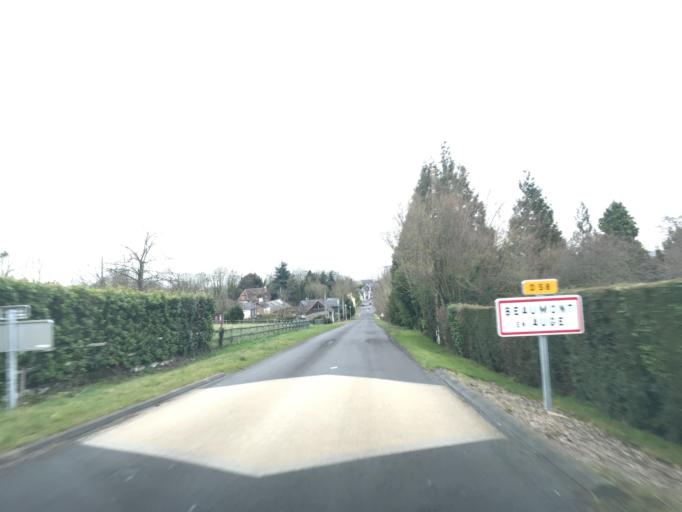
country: FR
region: Lower Normandy
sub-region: Departement du Calvados
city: Touques
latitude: 49.2733
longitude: 0.1082
